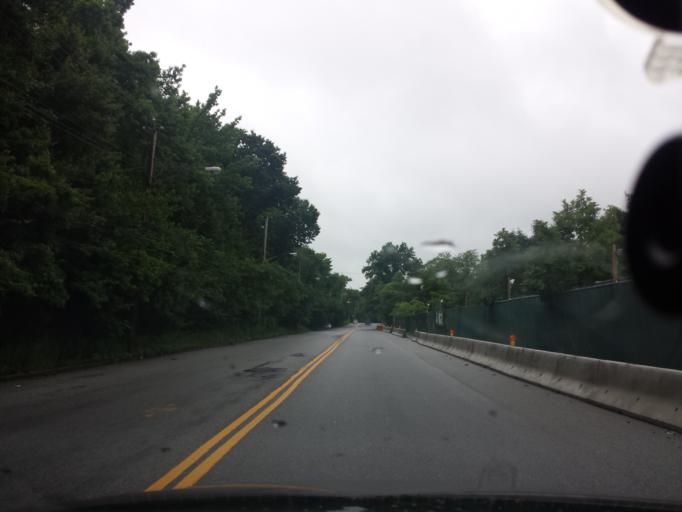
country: US
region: New York
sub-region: Richmond County
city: Staten Island
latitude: 40.5976
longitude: -74.1238
